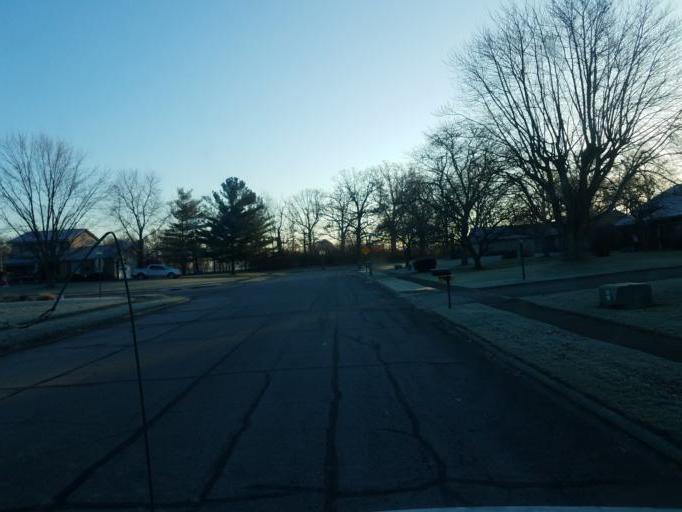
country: US
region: Ohio
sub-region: Marion County
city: Marion
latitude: 40.5697
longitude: -83.0942
